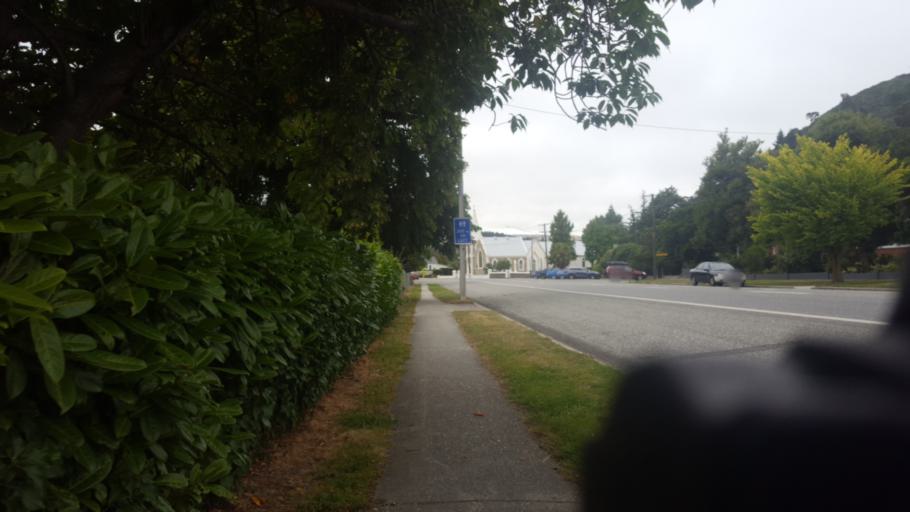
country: NZ
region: Otago
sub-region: Queenstown-Lakes District
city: Kingston
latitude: -45.5380
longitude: 169.3107
